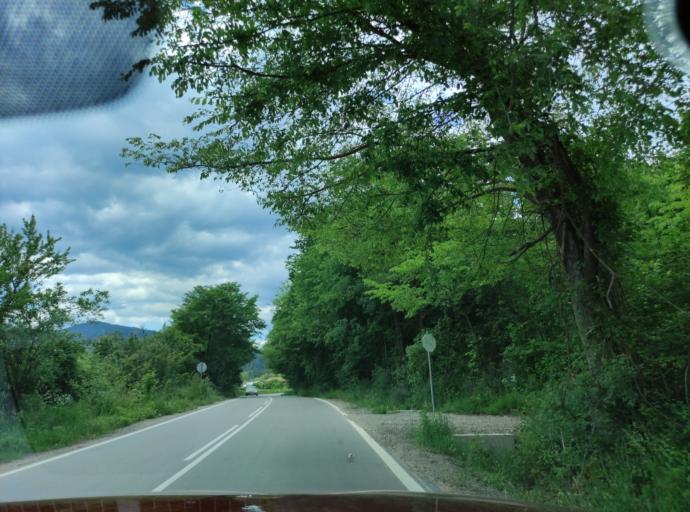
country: BG
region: Montana
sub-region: Obshtina Chiprovtsi
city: Chiprovtsi
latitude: 43.4372
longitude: 22.9465
